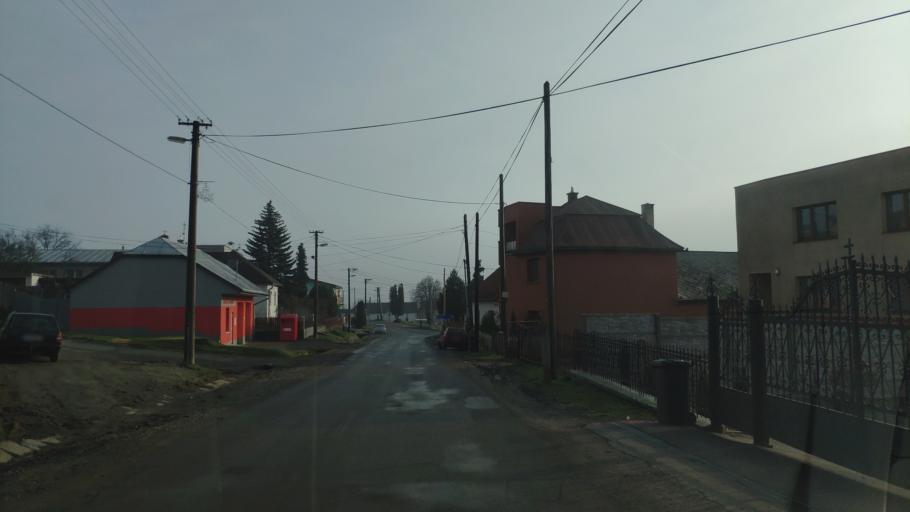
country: SK
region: Kosicky
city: Kosice
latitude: 48.7058
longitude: 21.4094
